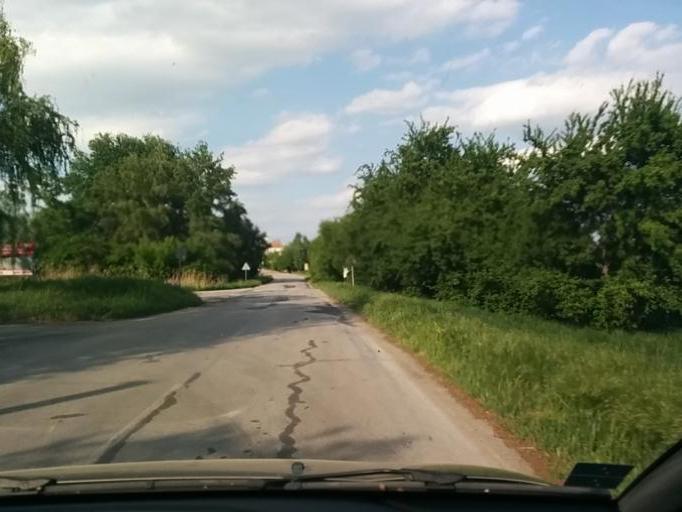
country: SK
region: Trnavsky
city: Sladkovicovo
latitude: 48.2281
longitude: 17.5668
